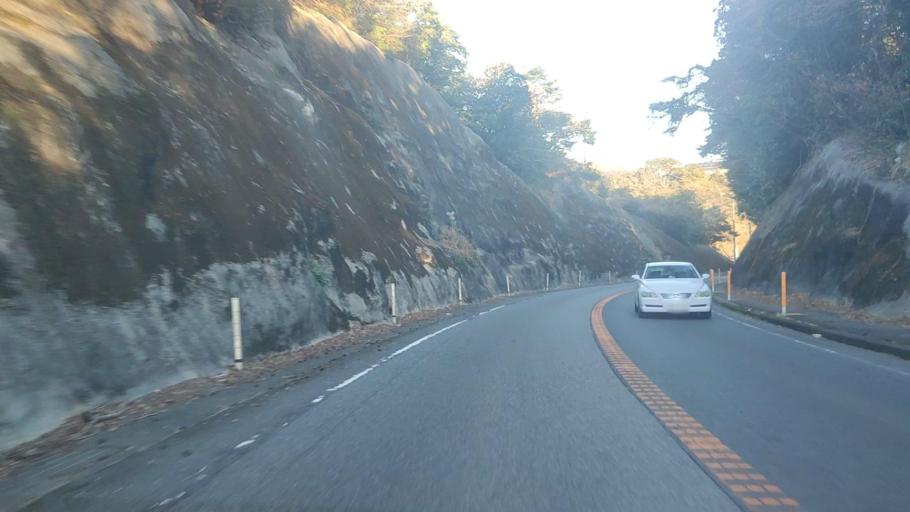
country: JP
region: Miyazaki
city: Nobeoka
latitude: 32.3473
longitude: 131.6226
